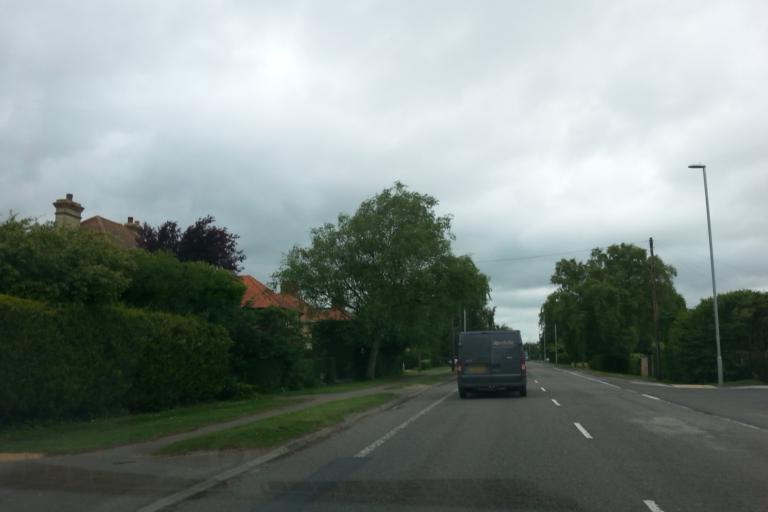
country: GB
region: England
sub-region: Cambridgeshire
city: Grantchester
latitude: 52.1623
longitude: 0.1230
